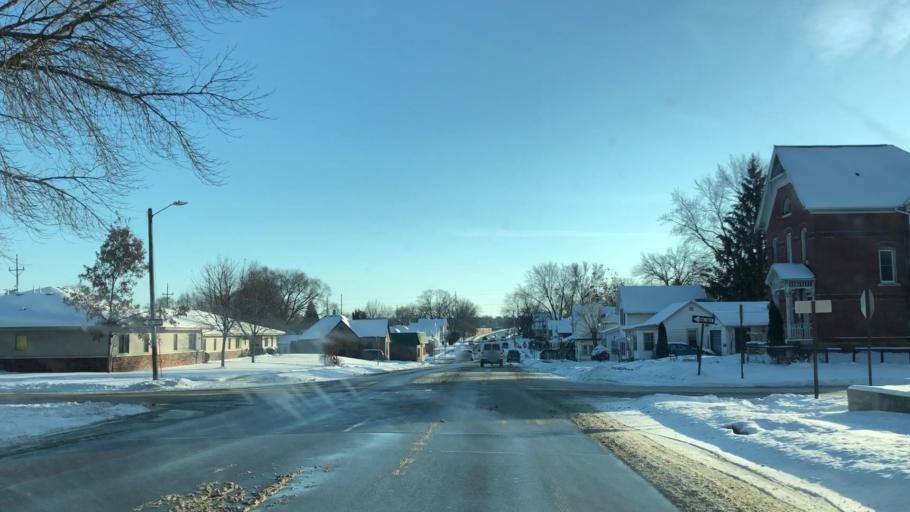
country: US
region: Iowa
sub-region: Marshall County
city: Marshalltown
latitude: 42.0469
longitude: -92.9179
